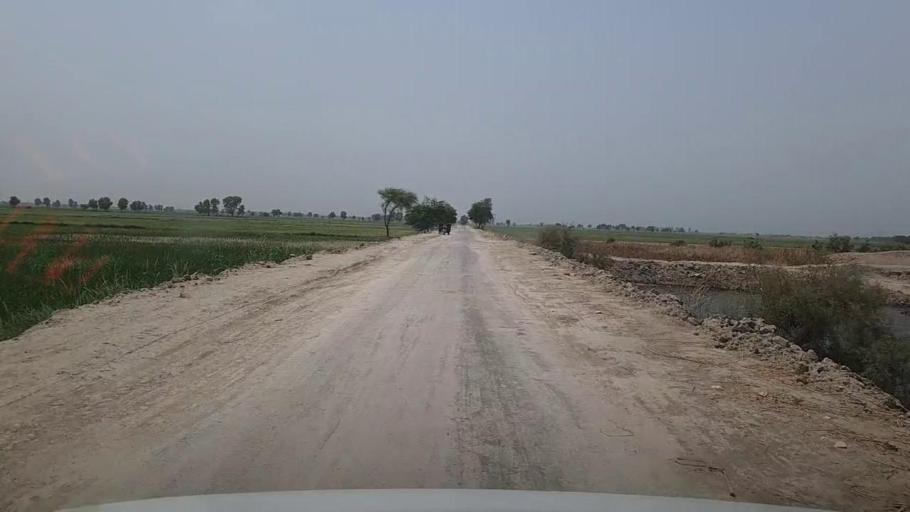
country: PK
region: Sindh
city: Sita Road
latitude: 27.0900
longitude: 67.9139
